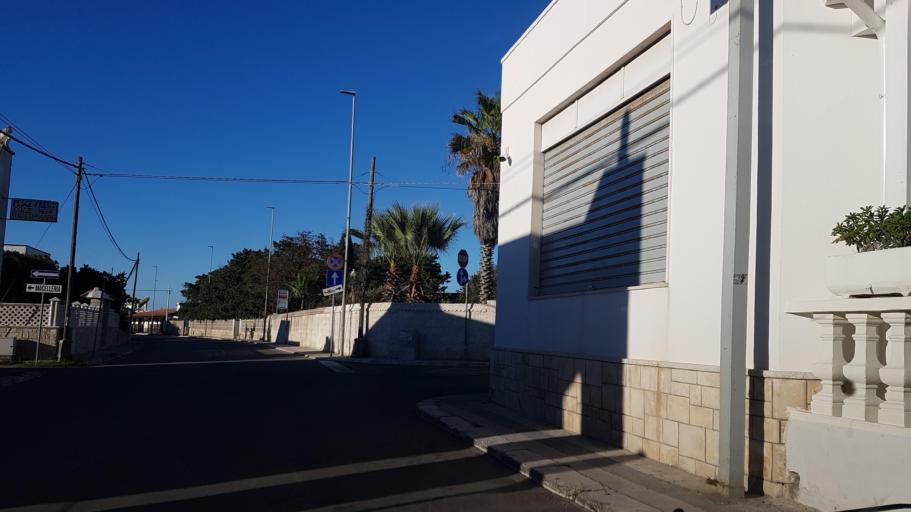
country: IT
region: Apulia
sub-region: Provincia di Lecce
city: Giorgilorio
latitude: 40.4654
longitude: 18.1952
